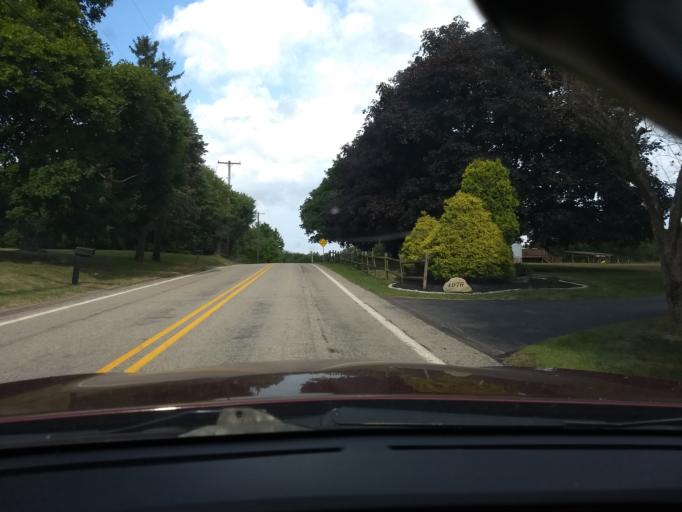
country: US
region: Pennsylvania
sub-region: Allegheny County
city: Curtisville
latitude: 40.6595
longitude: -79.8459
